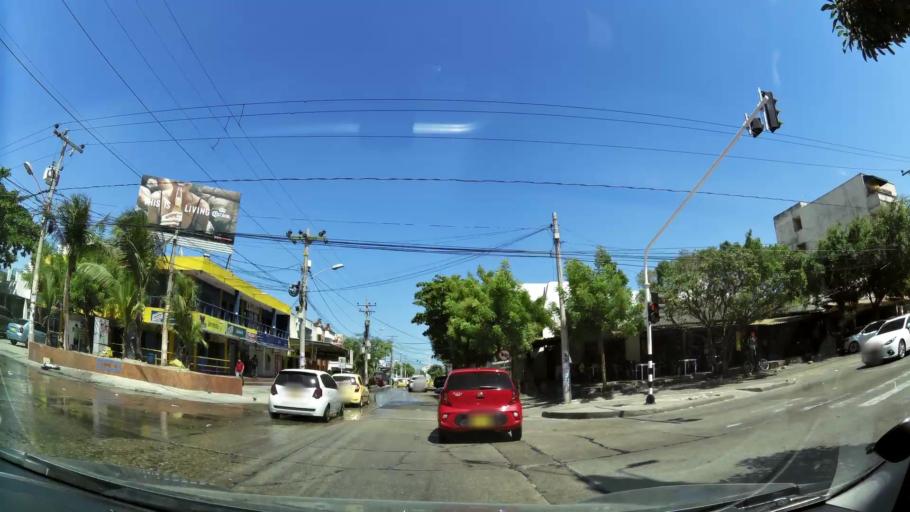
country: CO
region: Atlantico
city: Barranquilla
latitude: 10.9929
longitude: -74.8093
